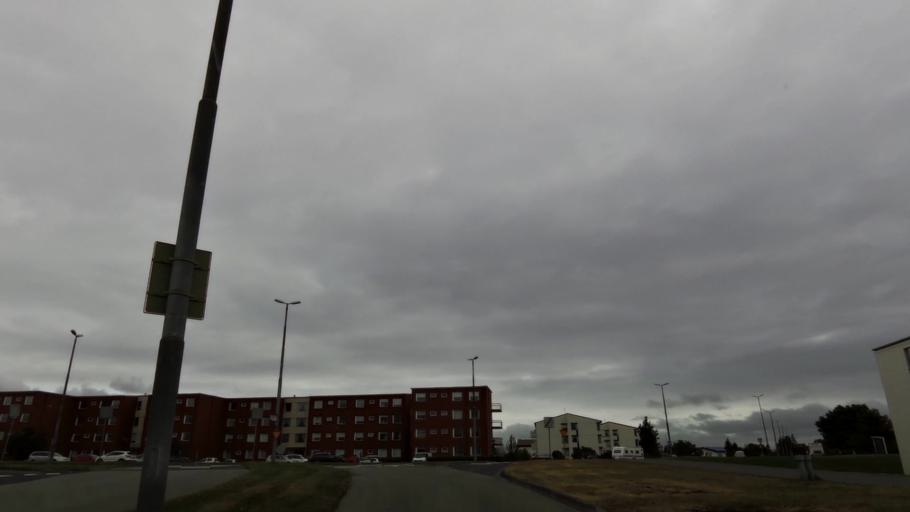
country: IS
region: Capital Region
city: Hafnarfjoerdur
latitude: 64.0801
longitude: -21.9618
